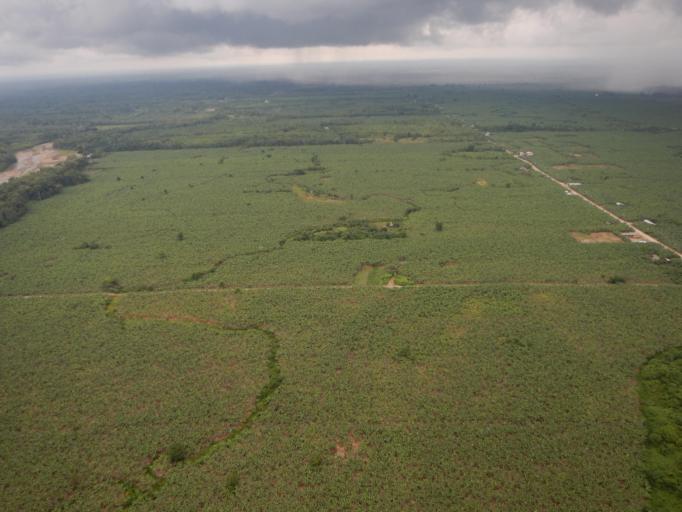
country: BO
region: Cochabamba
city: Chimore
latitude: -17.1948
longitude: -64.7075
